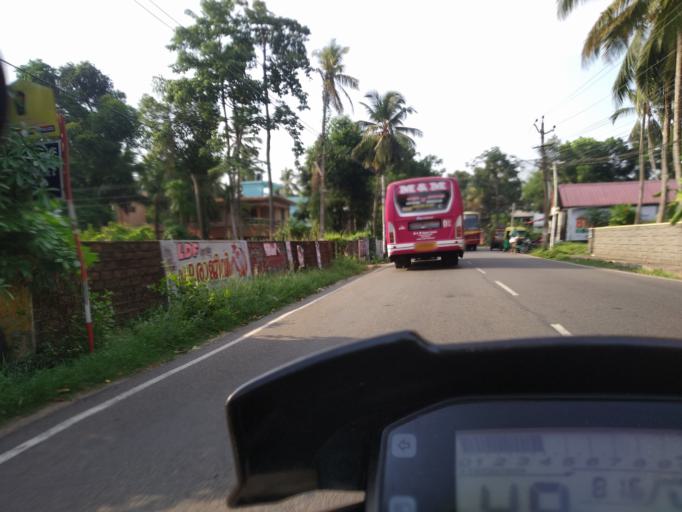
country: IN
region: Kerala
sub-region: Alappuzha
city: Arukutti
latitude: 9.9405
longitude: 76.3508
